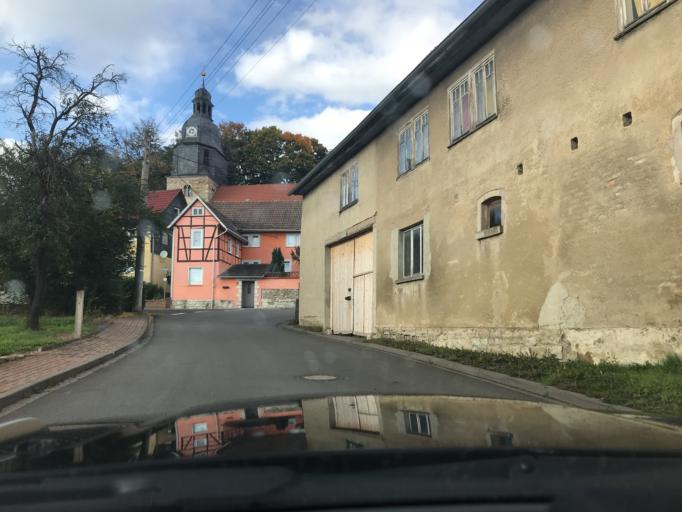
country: DE
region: Thuringia
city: Mulverstedt
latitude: 51.1210
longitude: 10.5078
